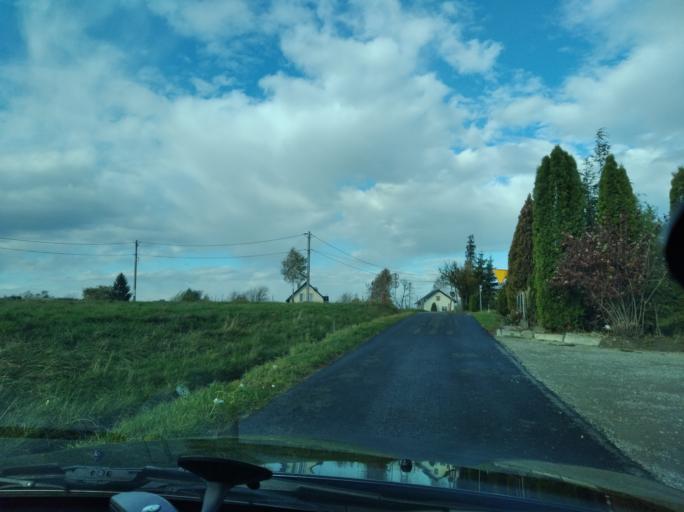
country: PL
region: Subcarpathian Voivodeship
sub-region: Powiat debicki
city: Debica
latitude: 50.0274
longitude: 21.4642
